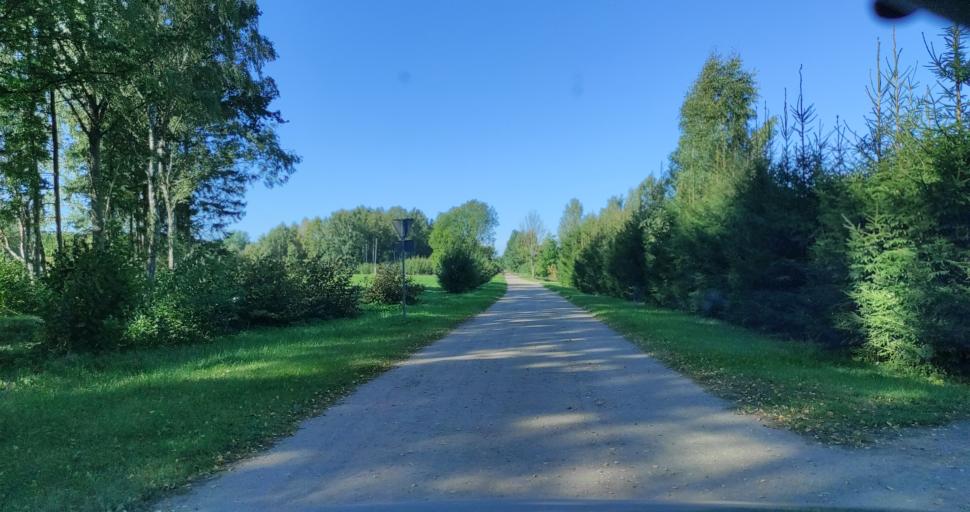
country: LV
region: Kuldigas Rajons
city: Kuldiga
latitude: 56.9726
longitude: 21.9302
